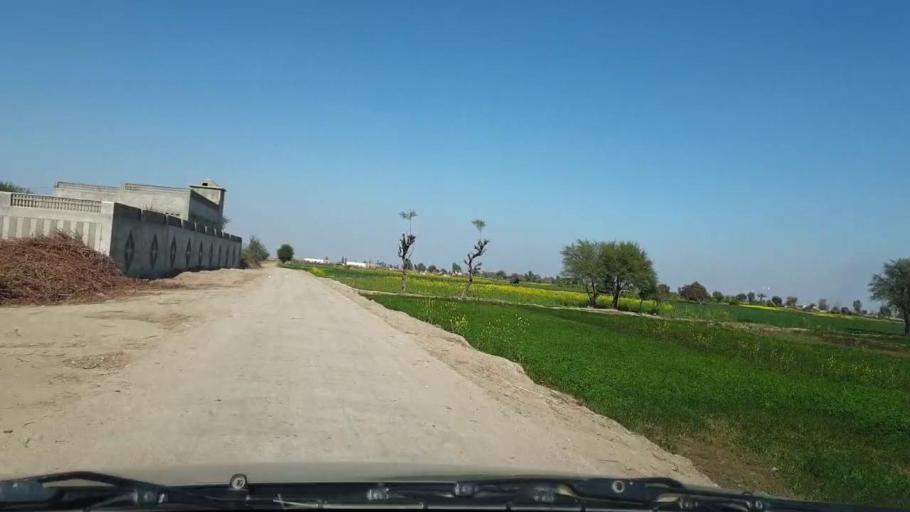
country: PK
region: Sindh
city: Khadro
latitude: 26.1457
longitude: 68.7951
